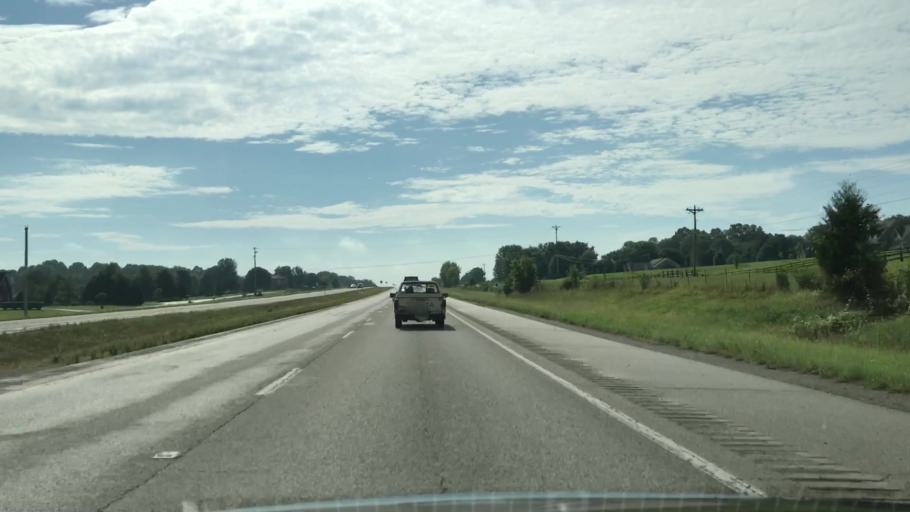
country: US
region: Kentucky
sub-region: Warren County
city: Plano
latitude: 36.8938
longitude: -86.3780
